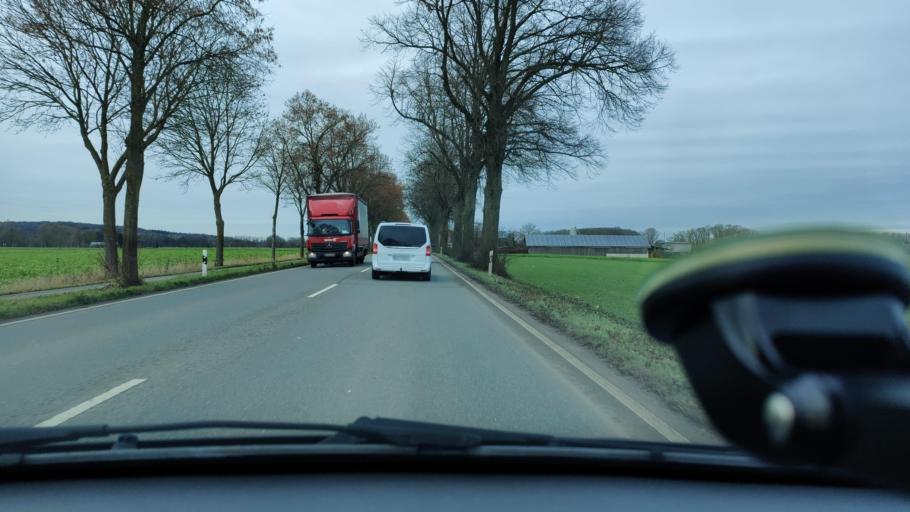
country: DE
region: North Rhine-Westphalia
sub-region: Regierungsbezirk Dusseldorf
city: Xanten
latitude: 51.6840
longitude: 6.4077
